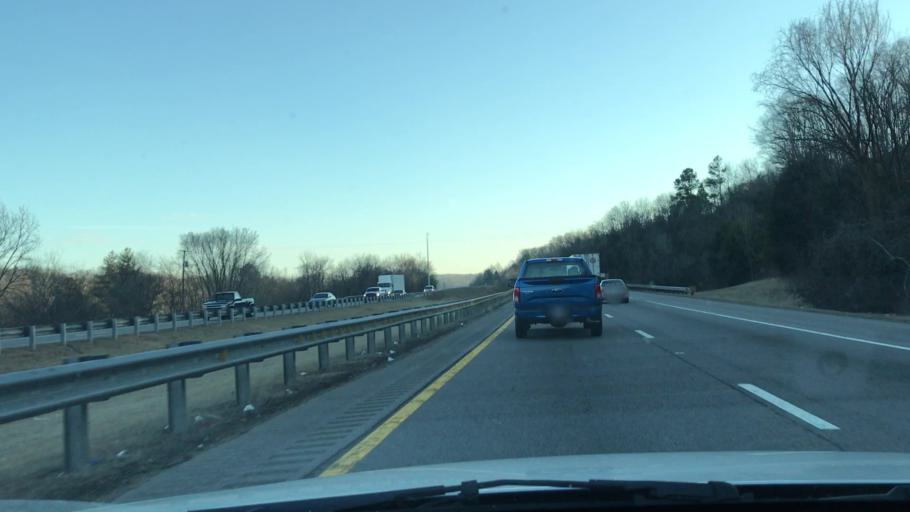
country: US
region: Tennessee
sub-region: Sumner County
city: Millersville
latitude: 36.3823
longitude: -86.7145
